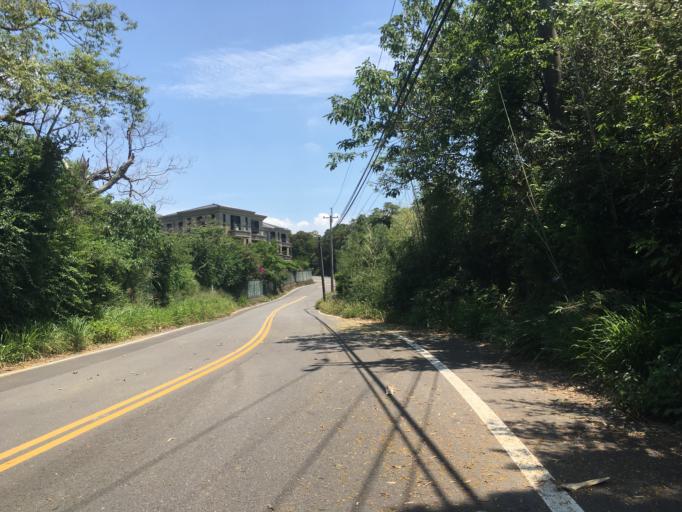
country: TW
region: Taiwan
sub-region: Hsinchu
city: Hsinchu
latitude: 24.7391
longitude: 120.9849
